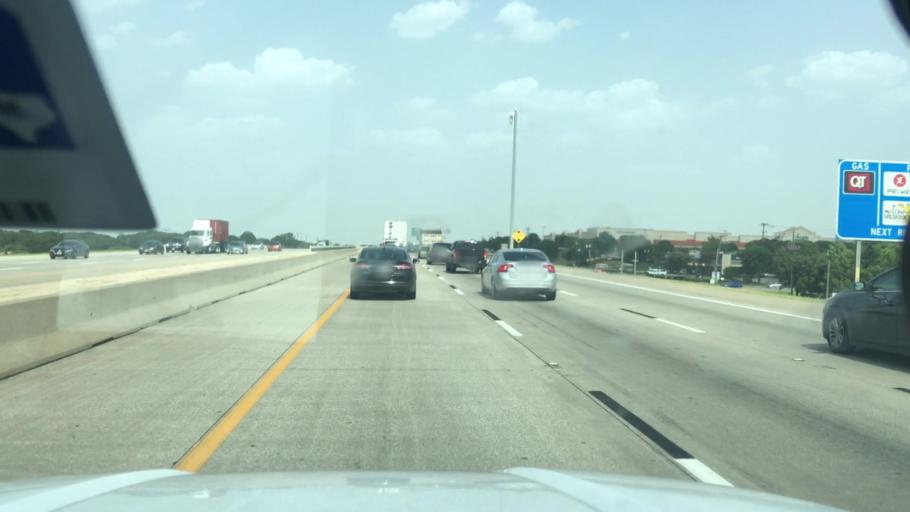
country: US
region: Texas
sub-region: Tarrant County
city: Southlake
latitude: 32.9436
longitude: -97.1185
